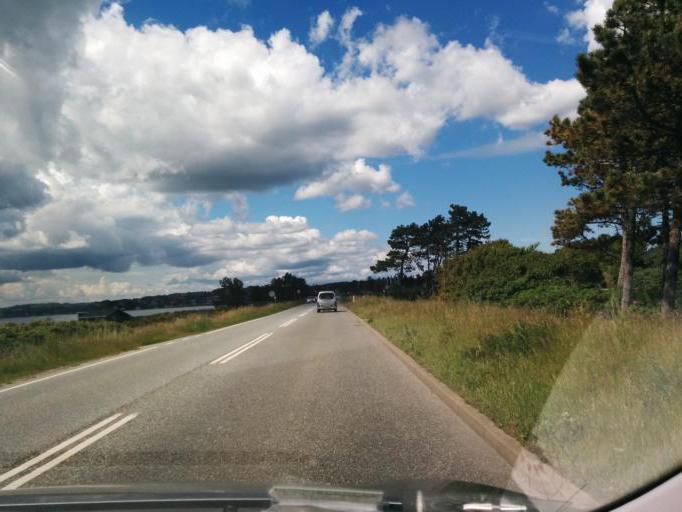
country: DK
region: Central Jutland
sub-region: Syddjurs Kommune
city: Ebeltoft
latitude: 56.2157
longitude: 10.6744
